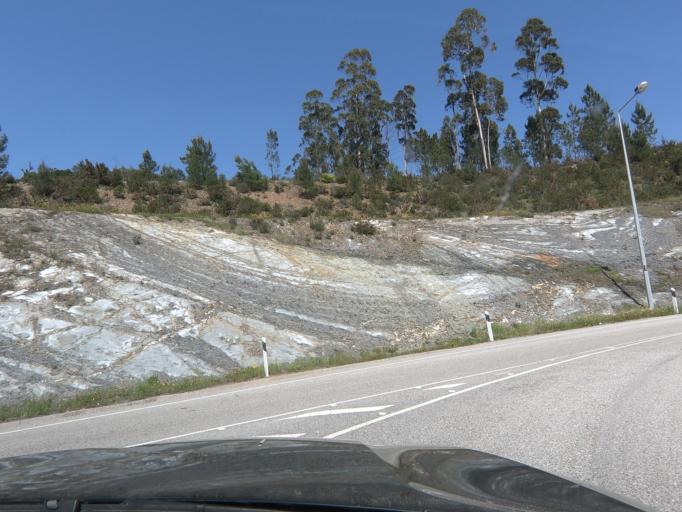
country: PT
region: Coimbra
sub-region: Vila Nova de Poiares
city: Poiares
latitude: 40.1743
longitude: -8.2675
